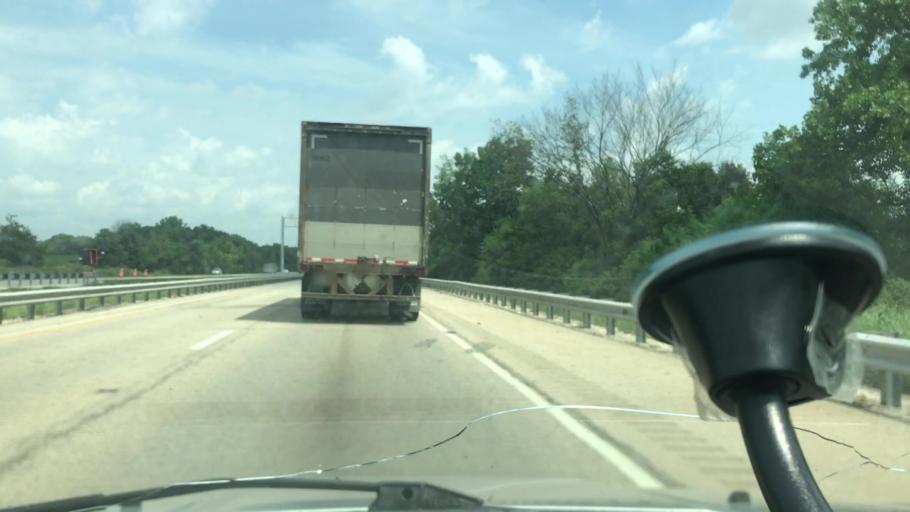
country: US
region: Illinois
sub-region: Peoria County
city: Bellevue
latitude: 40.7185
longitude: -89.6762
